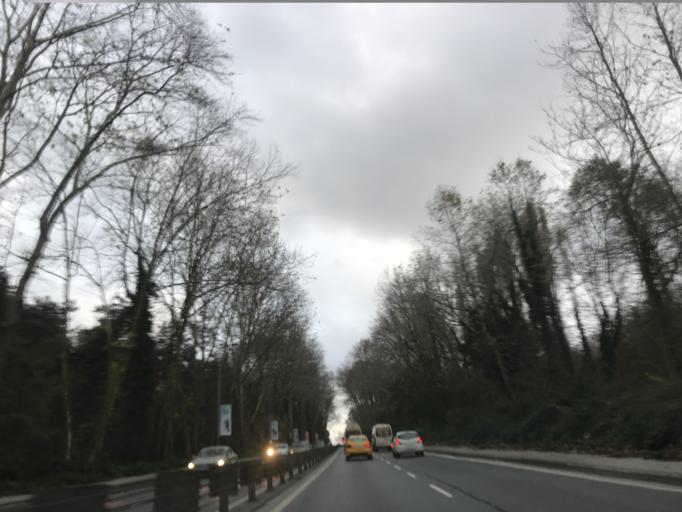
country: TR
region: Istanbul
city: Arikoey
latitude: 41.1464
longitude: 29.0279
